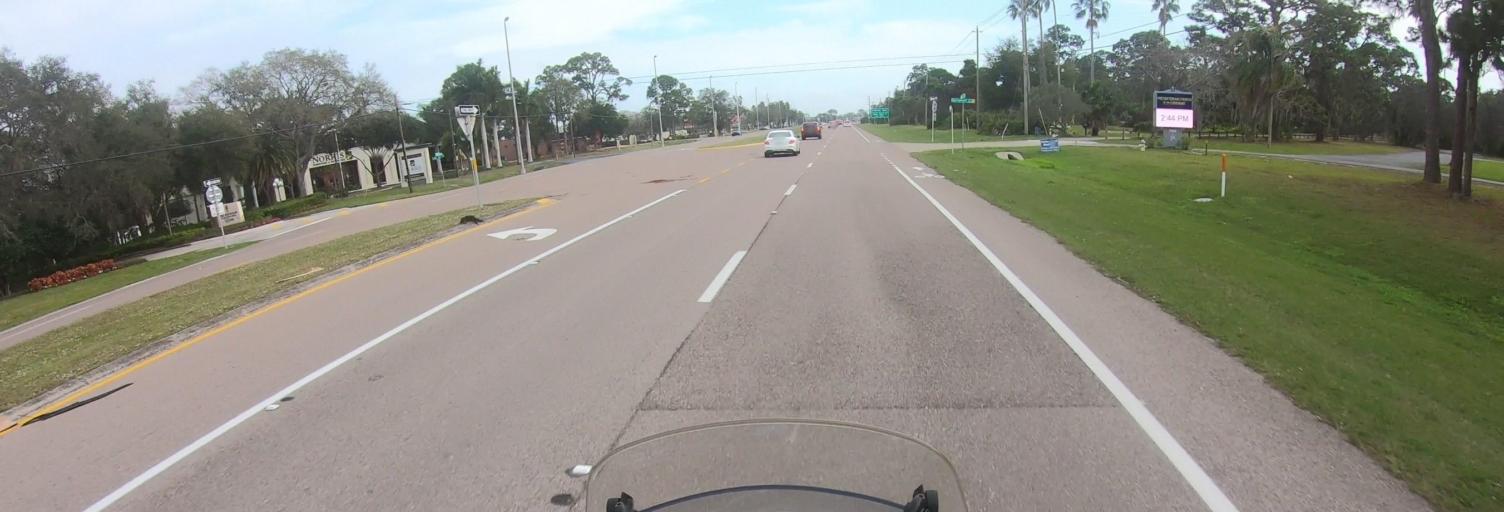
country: US
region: Florida
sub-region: Sarasota County
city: Vamo
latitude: 27.2367
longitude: -82.5022
